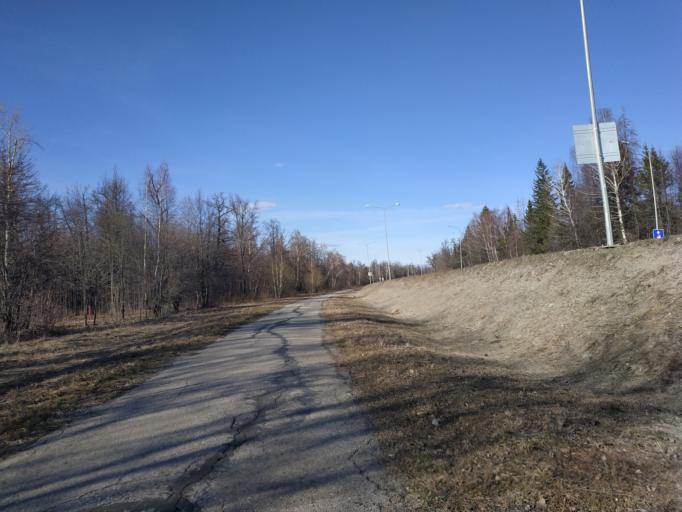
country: RU
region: Chuvashia
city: Ishley
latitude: 56.1230
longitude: 47.0610
